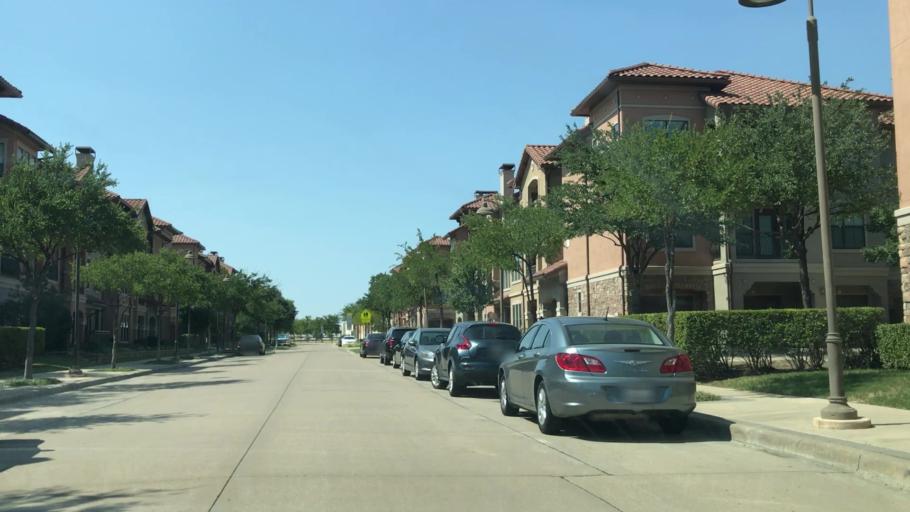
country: US
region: Texas
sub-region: Dallas County
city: Farmers Branch
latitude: 32.9005
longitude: -96.9368
